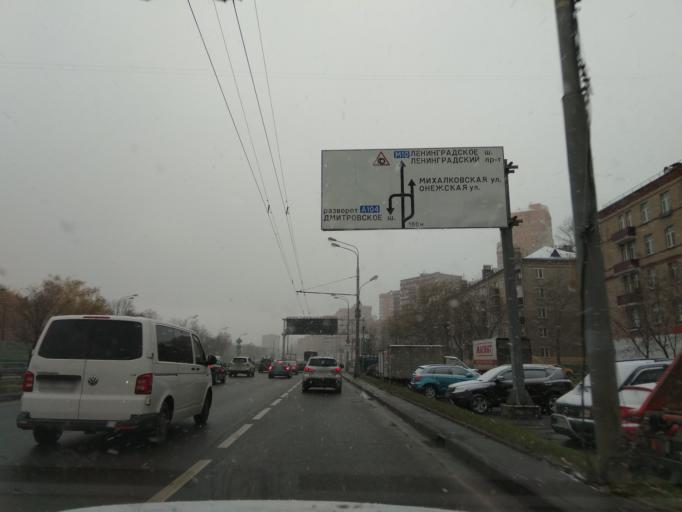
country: RU
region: Moscow
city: Likhobory
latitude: 55.8387
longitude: 37.5443
